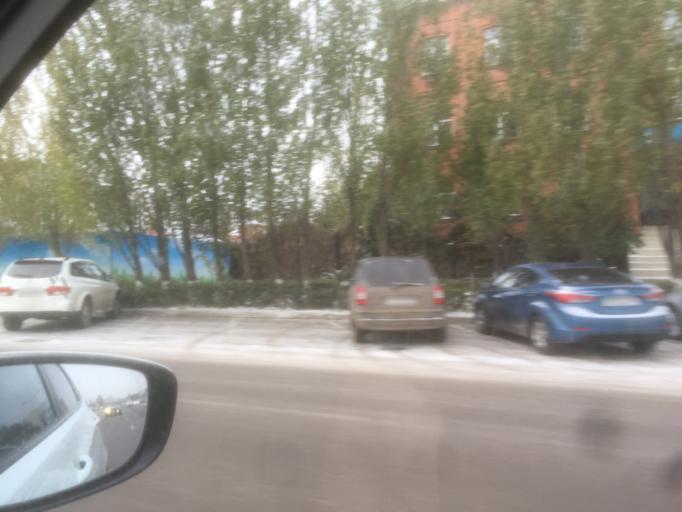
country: KZ
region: Astana Qalasy
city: Astana
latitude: 51.1486
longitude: 71.4580
